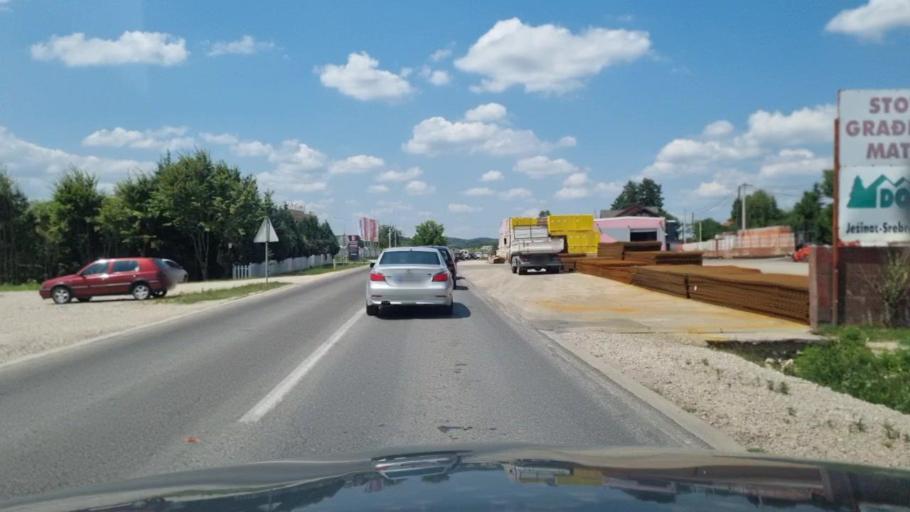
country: BA
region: Federation of Bosnia and Herzegovina
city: Srebrenik
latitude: 44.7266
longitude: 18.4832
